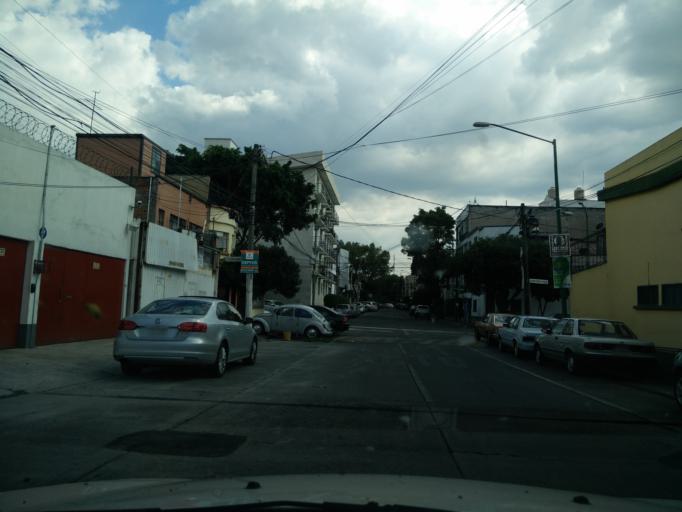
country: MX
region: Mexico City
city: Colonia del Valle
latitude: 19.3775
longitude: -99.1564
